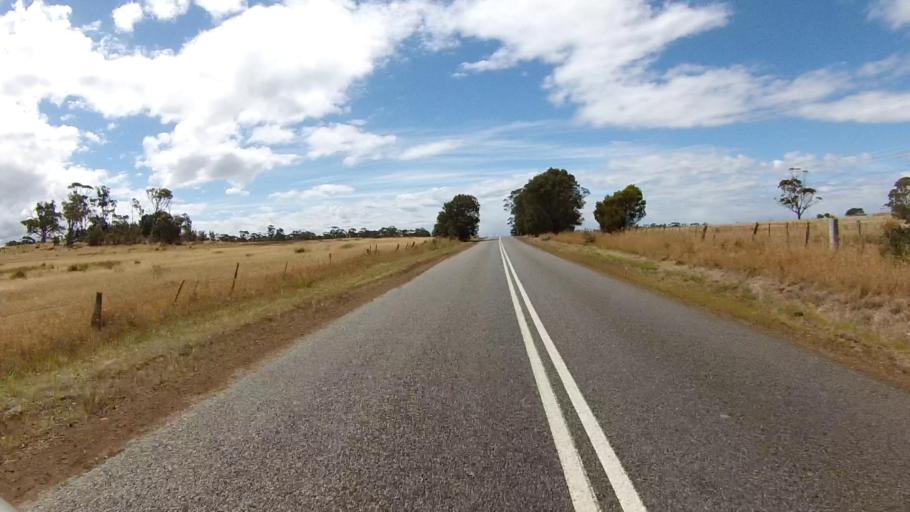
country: AU
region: Tasmania
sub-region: Sorell
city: Sorell
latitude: -42.2917
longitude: 147.9905
